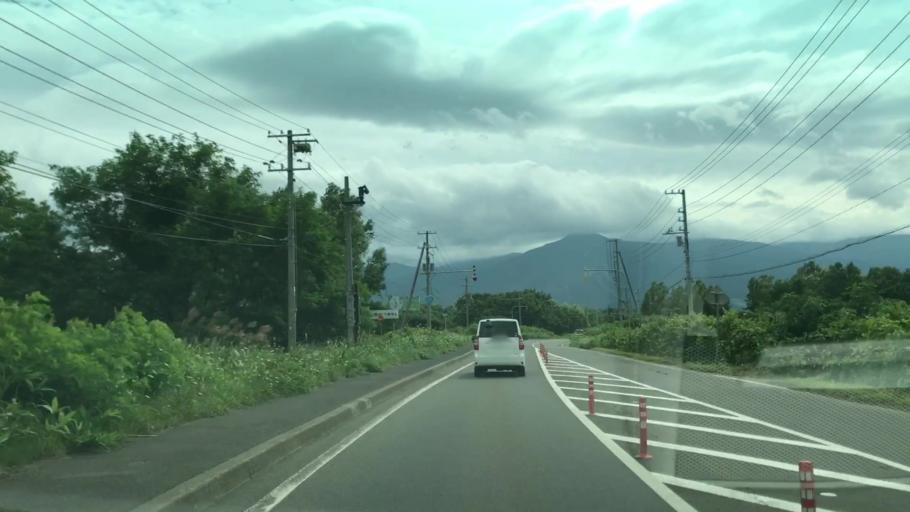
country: JP
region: Hokkaido
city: Iwanai
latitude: 43.0058
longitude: 140.5426
